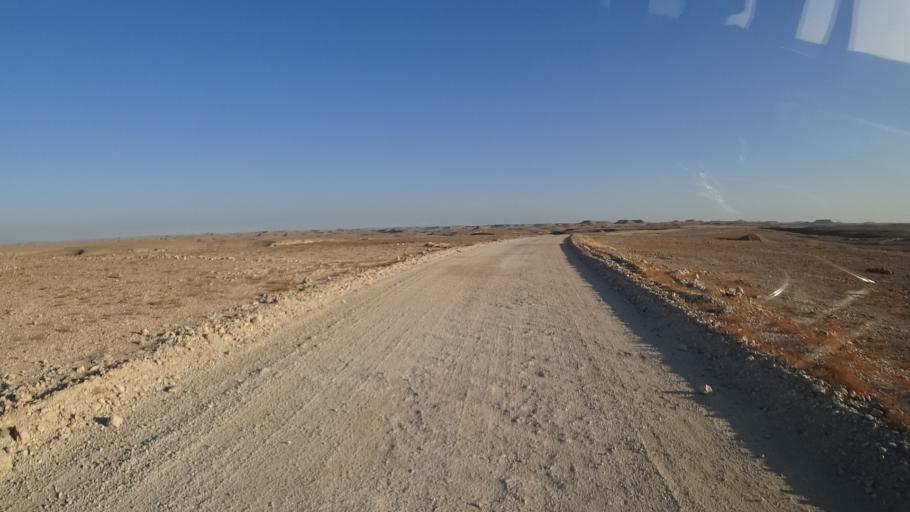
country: YE
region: Al Mahrah
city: Hawf
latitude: 17.1717
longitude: 53.3508
